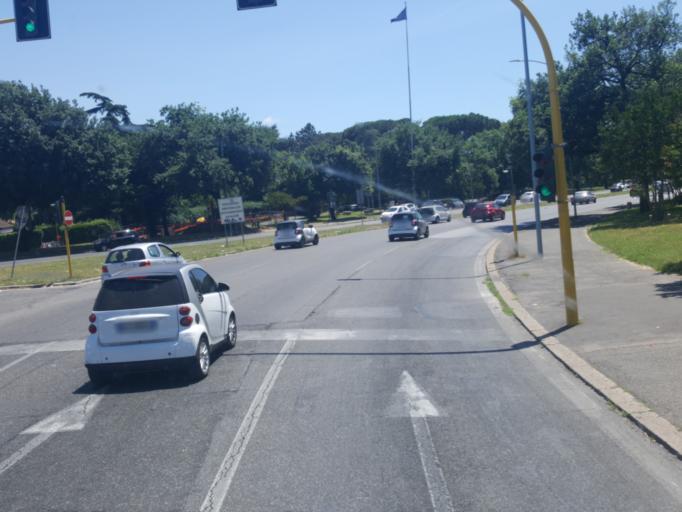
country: IT
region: Latium
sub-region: Citta metropolitana di Roma Capitale
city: Selcetta
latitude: 41.8230
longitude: 12.4649
